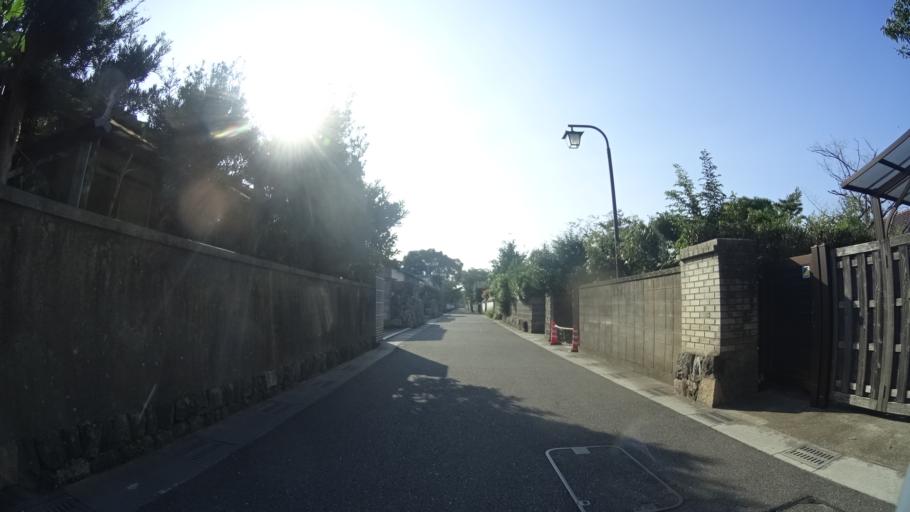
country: JP
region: Yamaguchi
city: Hagi
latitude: 34.4129
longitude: 131.3893
